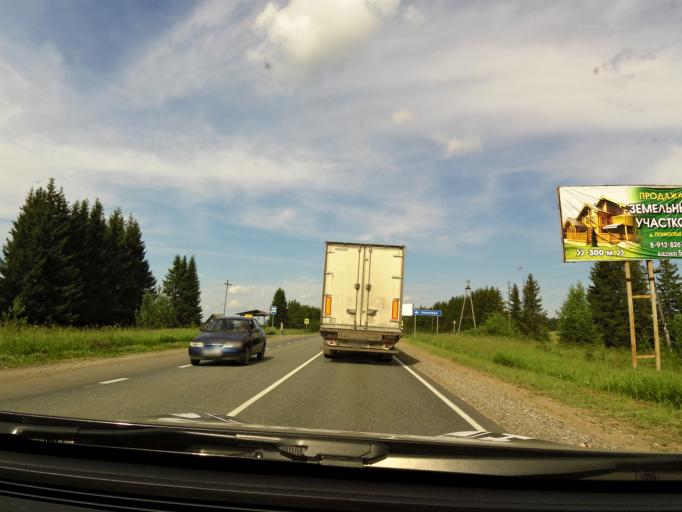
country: RU
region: Kirov
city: Slobodskoy
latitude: 58.7400
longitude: 50.2968
